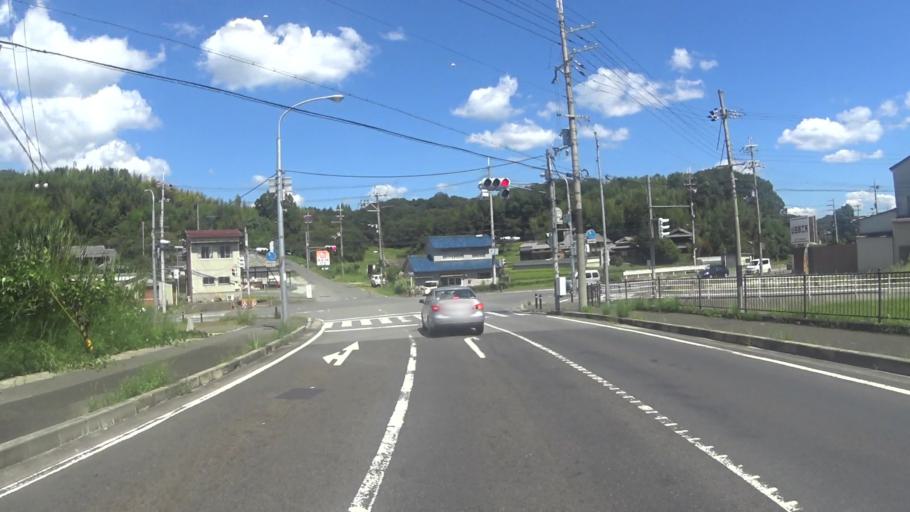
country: JP
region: Nara
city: Nara-shi
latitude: 34.7218
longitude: 135.8389
